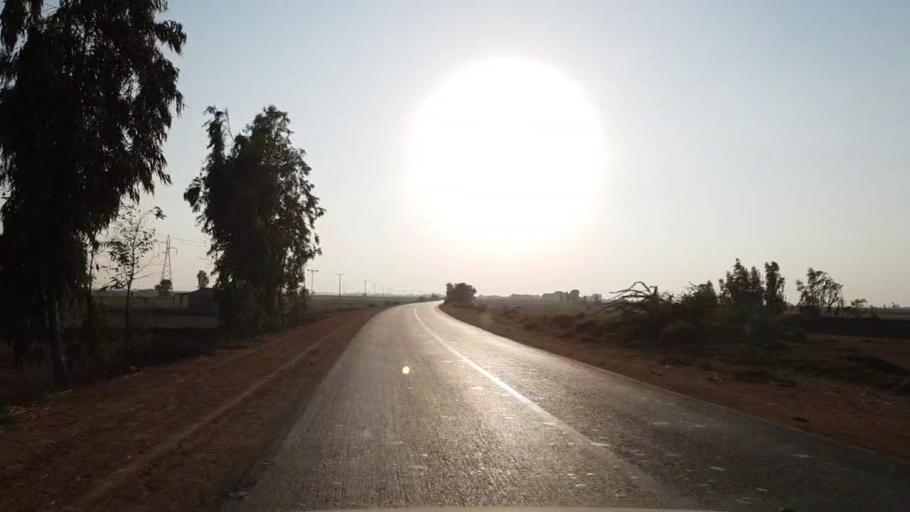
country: PK
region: Sindh
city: Daro Mehar
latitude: 24.6405
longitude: 68.1171
